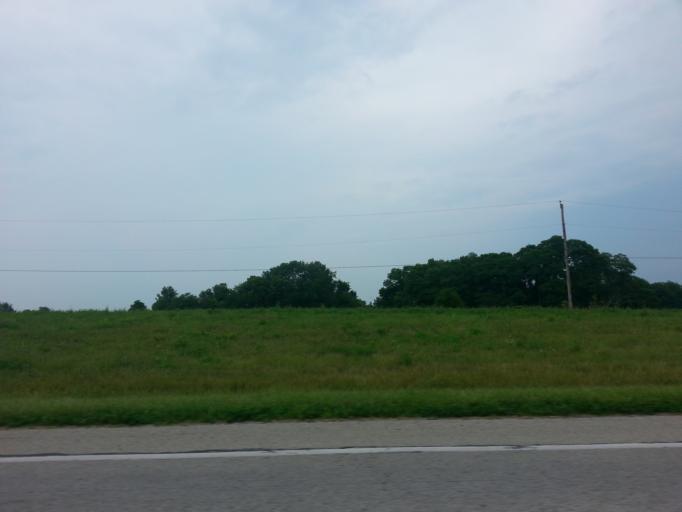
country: US
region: Ohio
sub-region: Brown County
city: Georgetown
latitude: 38.8533
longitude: -83.8526
